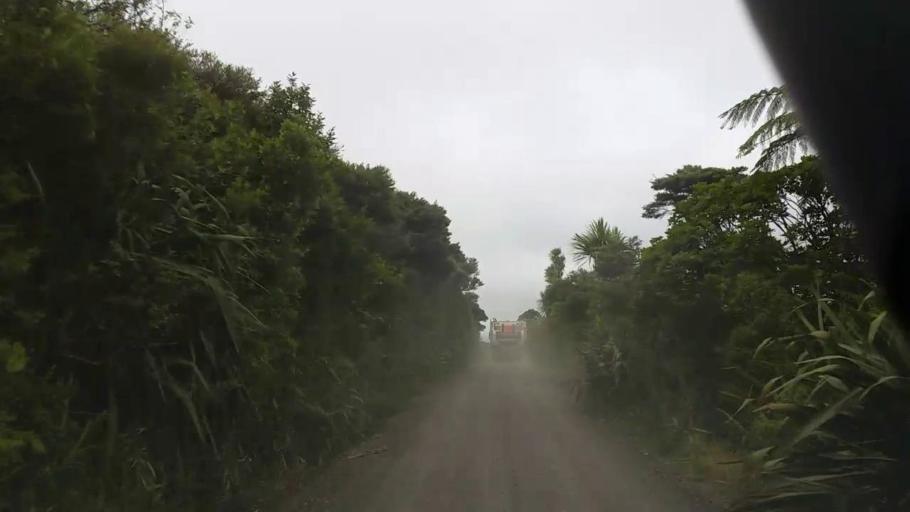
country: NZ
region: Auckland
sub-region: Auckland
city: Muriwai Beach
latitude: -36.9273
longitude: 174.4787
